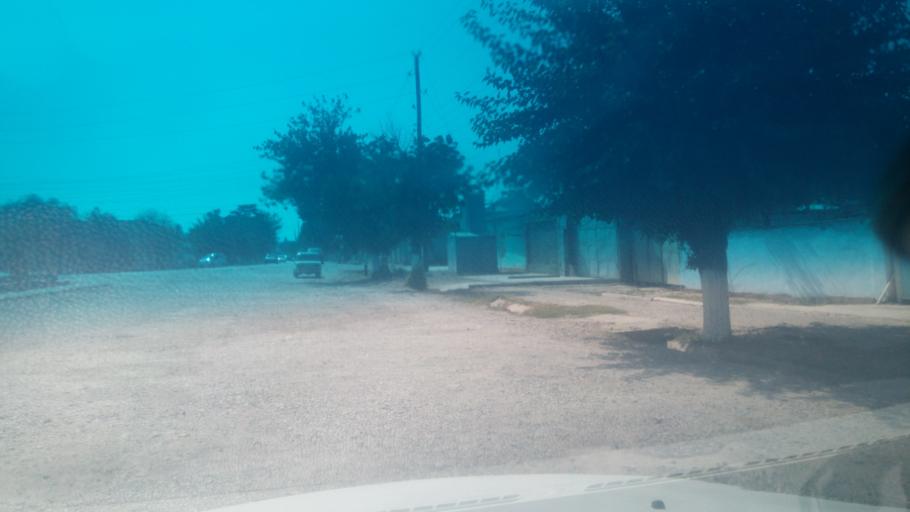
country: UZ
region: Sirdaryo
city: Sirdaryo
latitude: 40.8534
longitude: 68.6584
